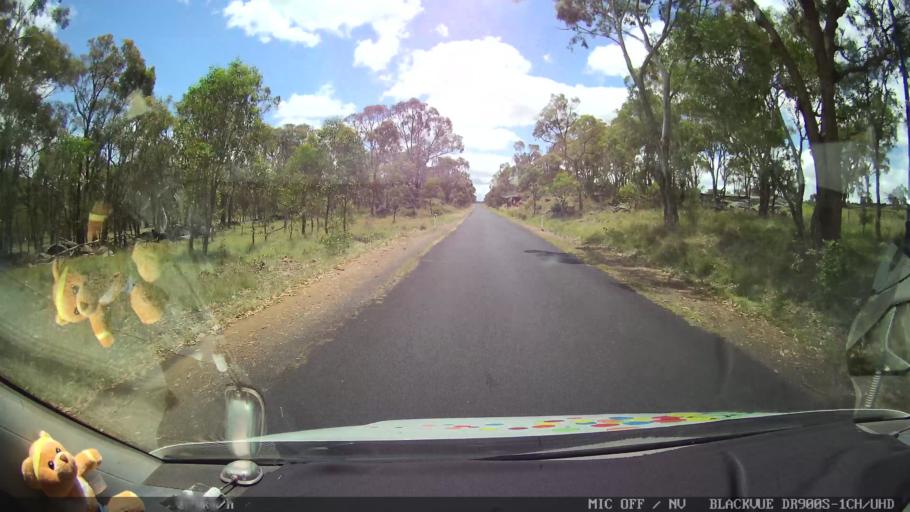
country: AU
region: New South Wales
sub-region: Glen Innes Severn
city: Glen Innes
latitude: -29.4318
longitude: 151.6883
